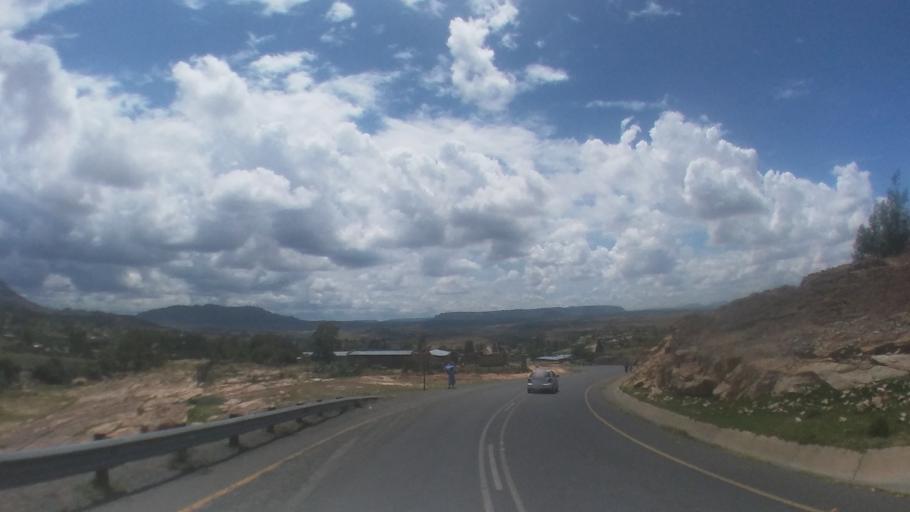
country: LS
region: Maseru
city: Maseru
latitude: -29.4219
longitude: 27.4705
